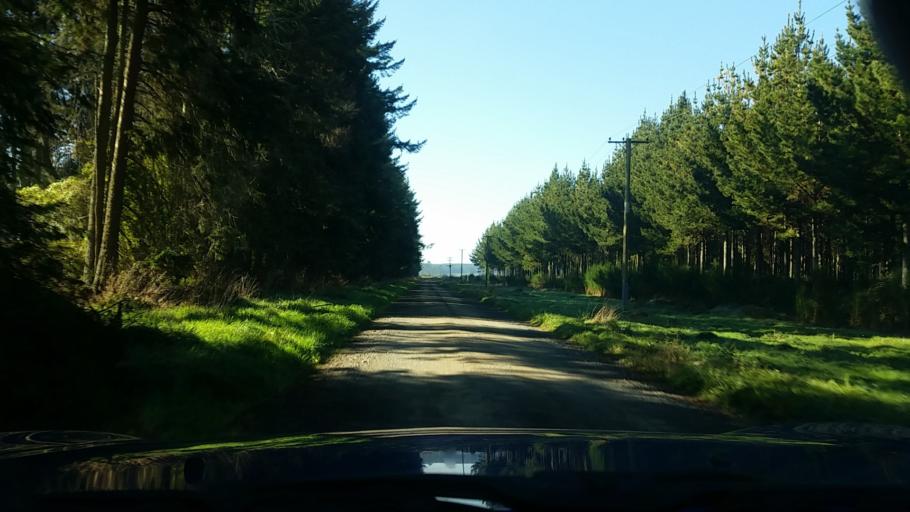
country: NZ
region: Bay of Plenty
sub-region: Whakatane District
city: Murupara
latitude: -38.3508
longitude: 176.5081
